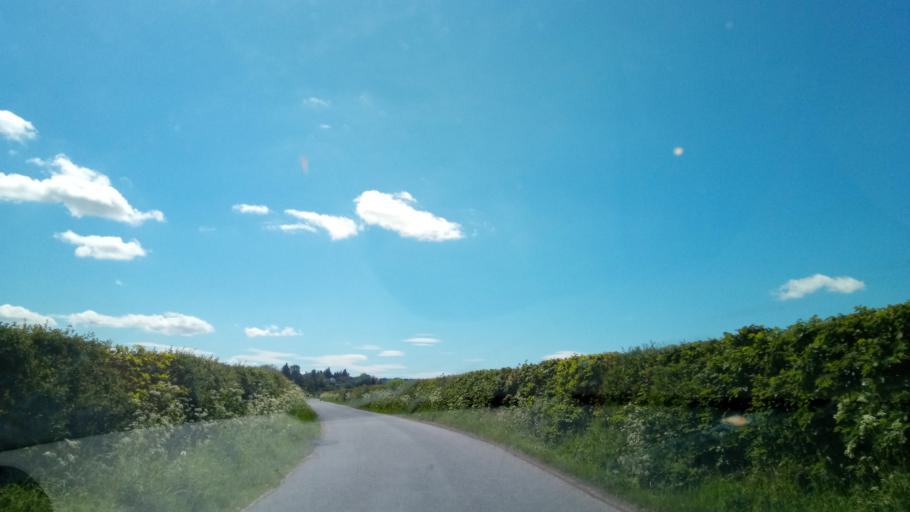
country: GB
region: Scotland
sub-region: The Scottish Borders
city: Saint Boswells
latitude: 55.4665
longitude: -2.6793
